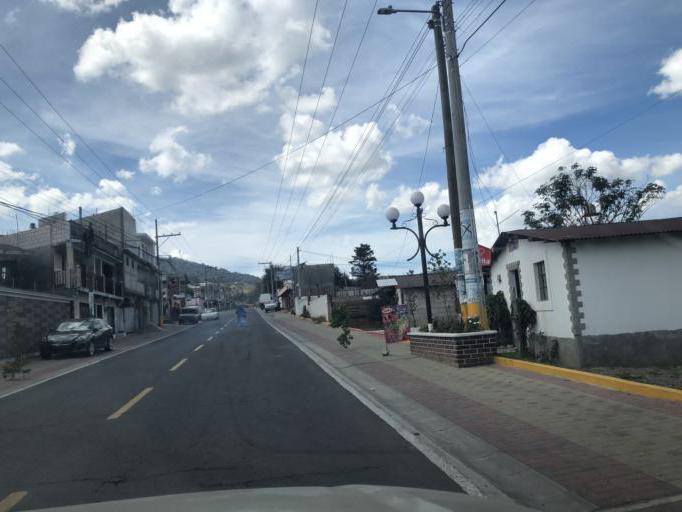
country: GT
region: Quetzaltenango
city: San Mateo
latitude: 14.8620
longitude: -91.5855
